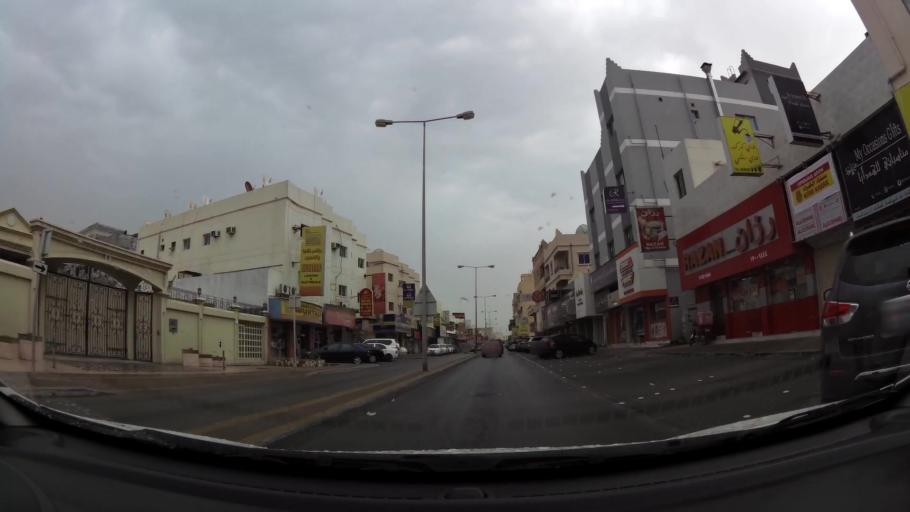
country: BH
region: Northern
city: Madinat `Isa
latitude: 26.1690
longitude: 50.5665
